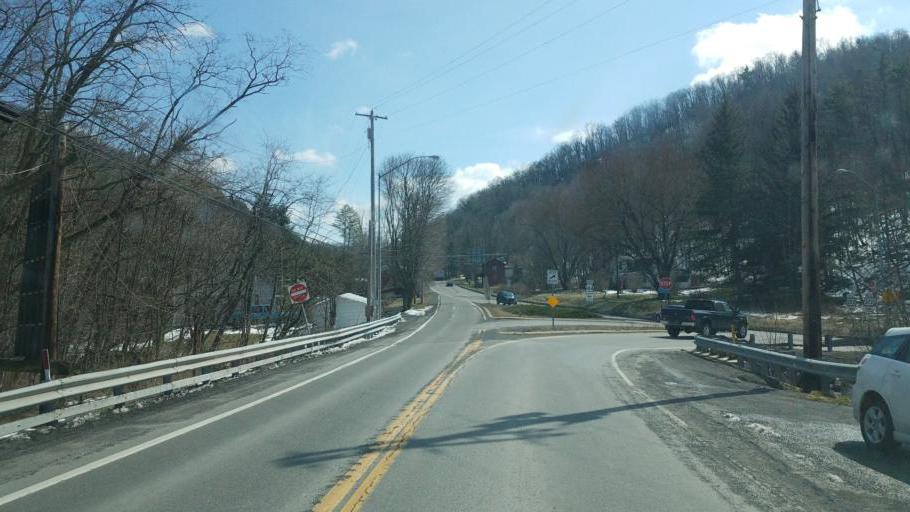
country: US
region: Pennsylvania
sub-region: Centre County
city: Centre Hall
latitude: 40.7952
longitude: -77.6251
